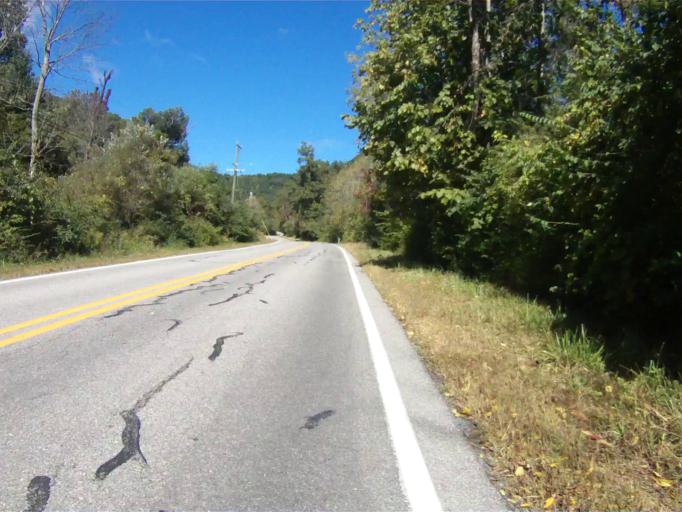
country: US
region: Pennsylvania
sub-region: Centre County
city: Park Forest Village
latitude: 40.8685
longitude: -77.8898
